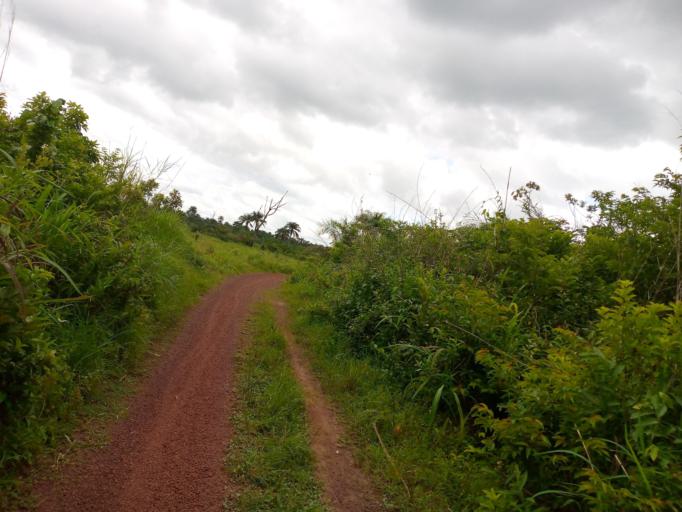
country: SL
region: Northern Province
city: Mange
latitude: 8.9861
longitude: -12.7261
